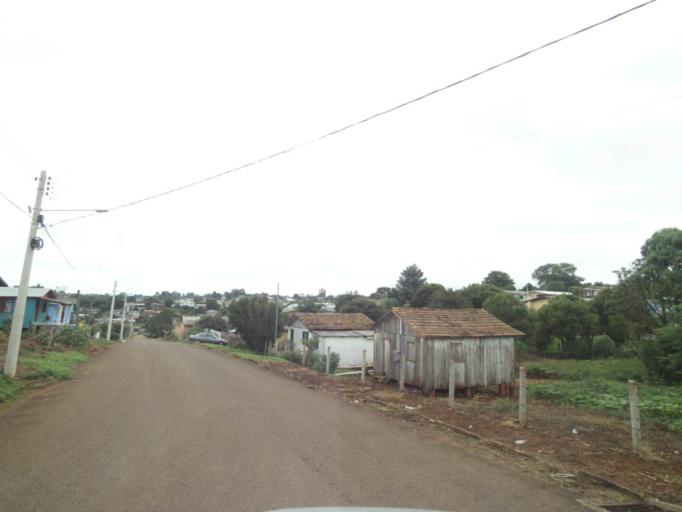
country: BR
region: Rio Grande do Sul
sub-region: Lagoa Vermelha
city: Lagoa Vermelha
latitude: -28.2182
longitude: -51.5389
